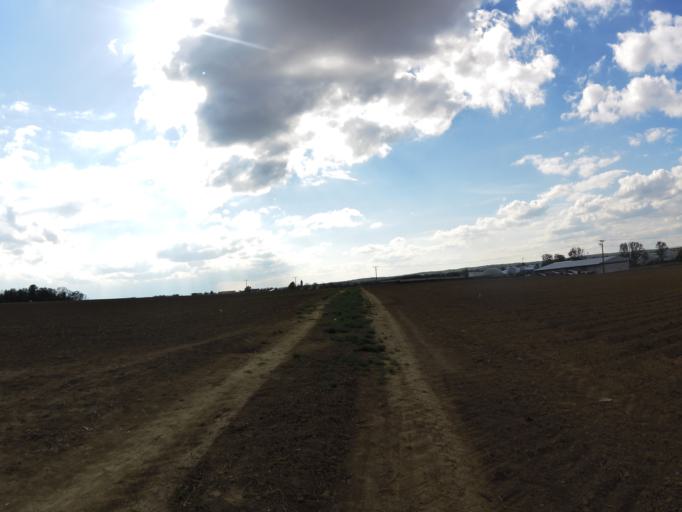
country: DE
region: Bavaria
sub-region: Regierungsbezirk Unterfranken
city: Unterpleichfeld
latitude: 49.8661
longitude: 10.0635
